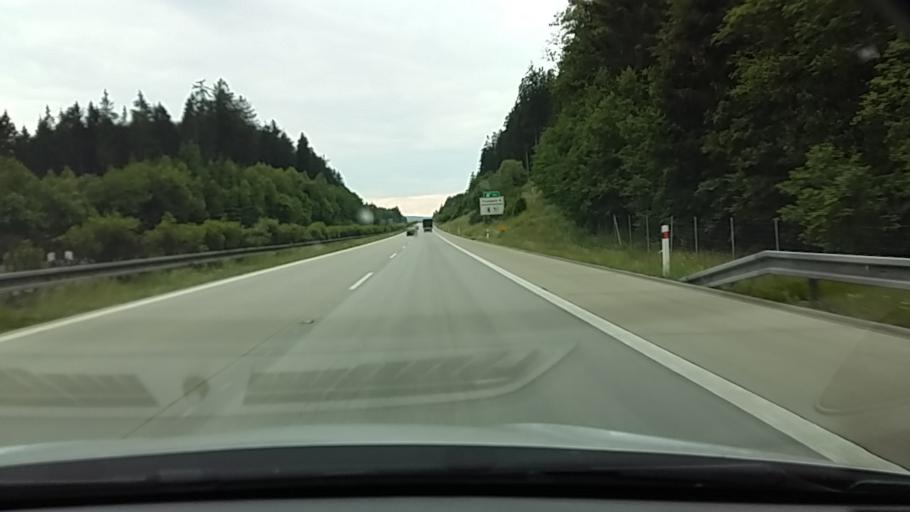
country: CZ
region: Plzensky
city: Primda
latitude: 49.6801
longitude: 12.6328
